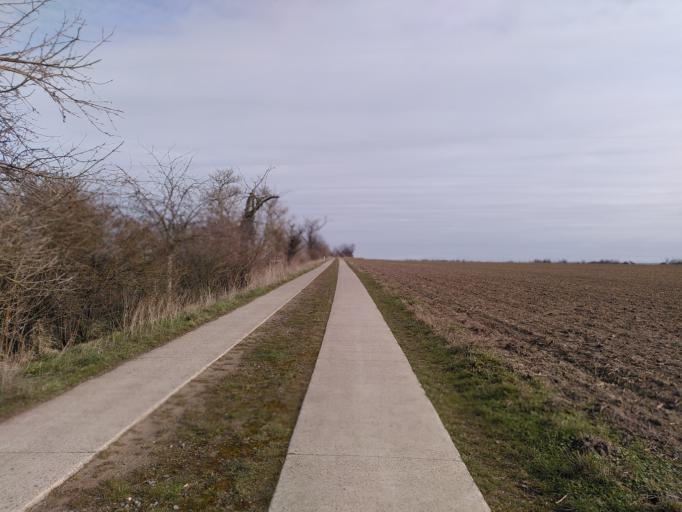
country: DE
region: Saxony-Anhalt
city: Gatersleben
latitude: 51.8065
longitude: 11.2681
